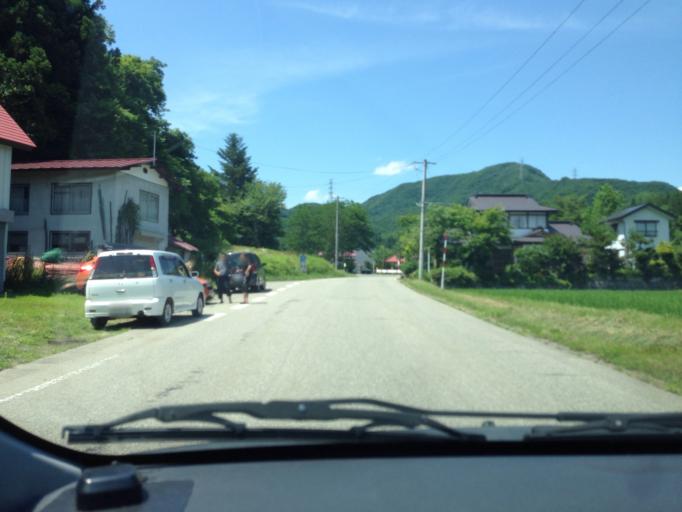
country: JP
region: Tochigi
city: Kuroiso
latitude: 37.2138
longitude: 139.7548
